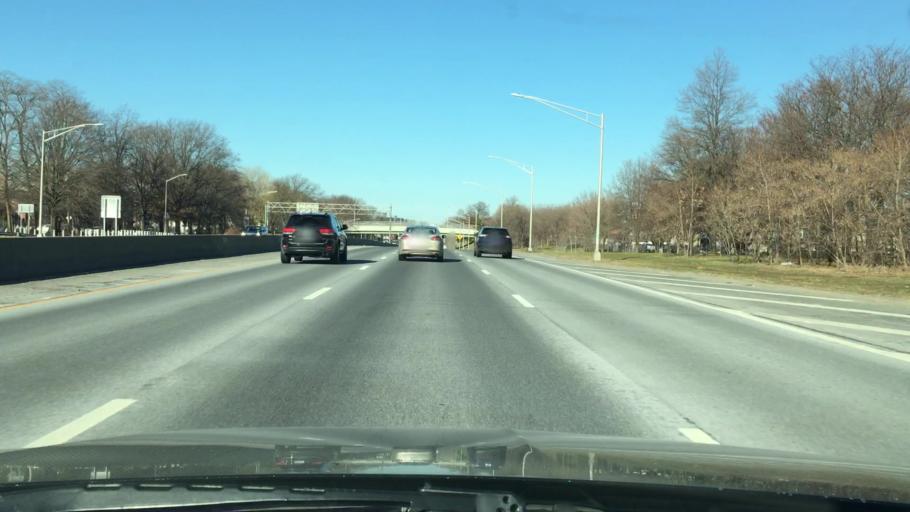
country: US
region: New York
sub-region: Bronx
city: The Bronx
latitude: 40.8295
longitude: -73.8189
